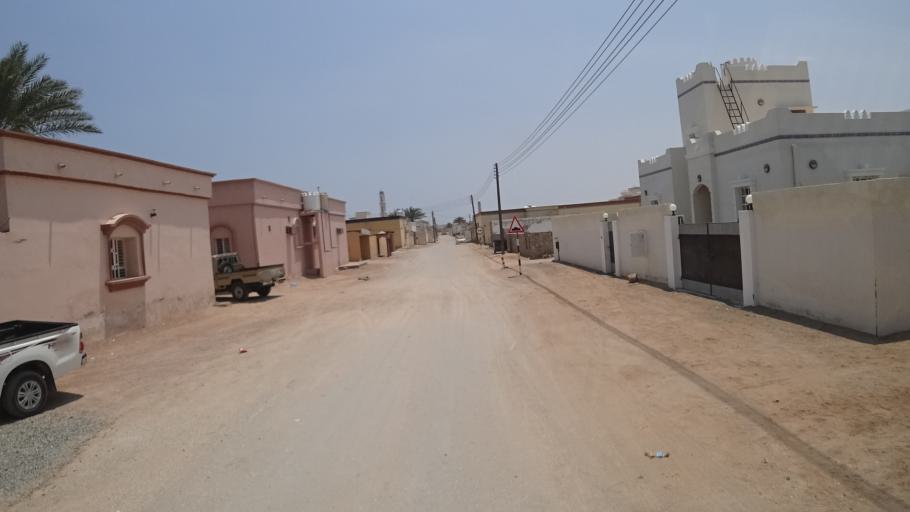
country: OM
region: Ash Sharqiyah
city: Sur
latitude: 22.5146
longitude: 59.7993
